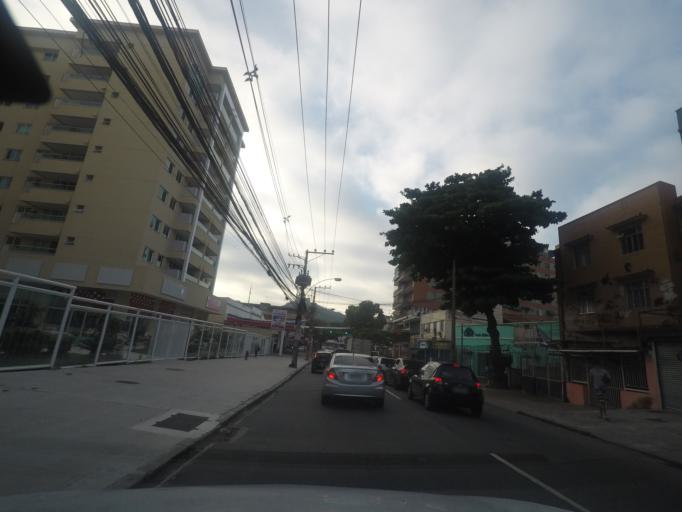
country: BR
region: Rio de Janeiro
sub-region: Duque De Caxias
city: Duque de Caxias
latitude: -22.8378
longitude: -43.2808
